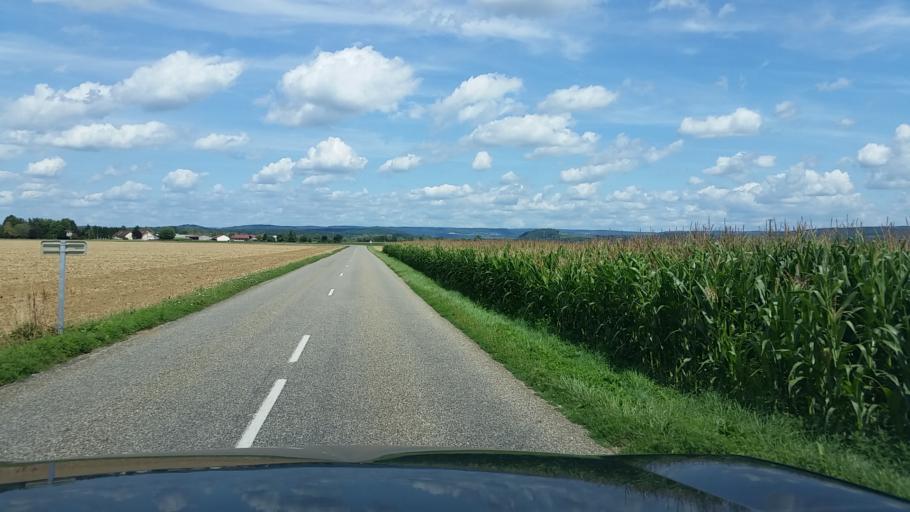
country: FR
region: Franche-Comte
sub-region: Departement du Jura
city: Bletterans
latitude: 46.7541
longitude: 5.4600
